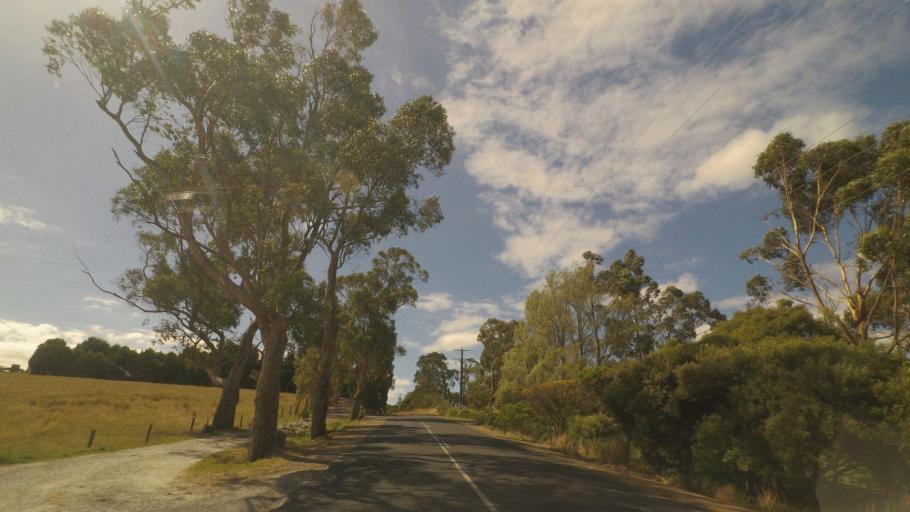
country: AU
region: Victoria
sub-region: Cardinia
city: Koo-Wee-Rup
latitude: -38.3236
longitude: 145.6714
